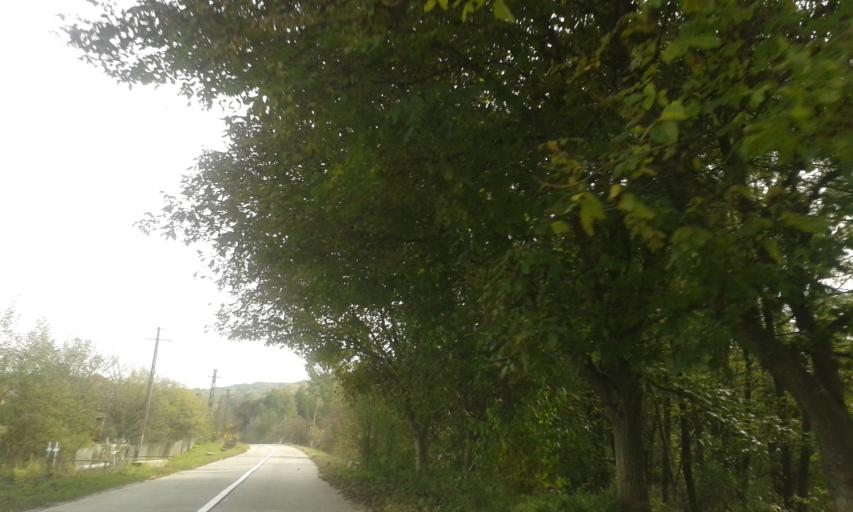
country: RO
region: Valcea
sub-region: Comuna Gradistea
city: Gradistea
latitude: 44.9071
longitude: 23.7936
